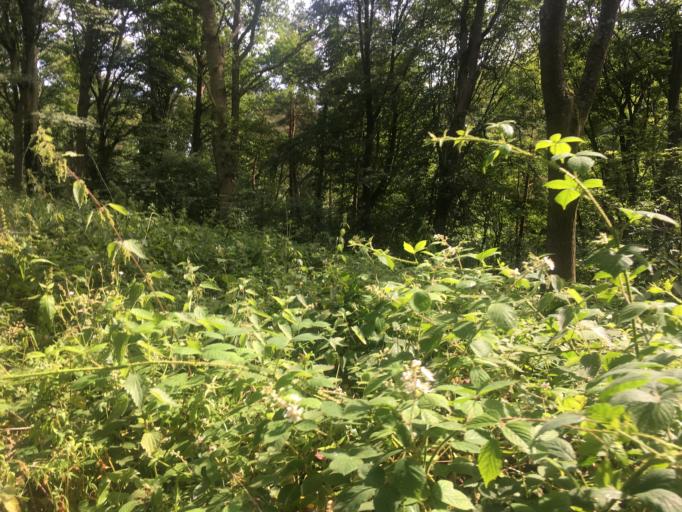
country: GB
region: England
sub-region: Sunderland
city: Washington
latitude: 54.8773
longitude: -1.5309
